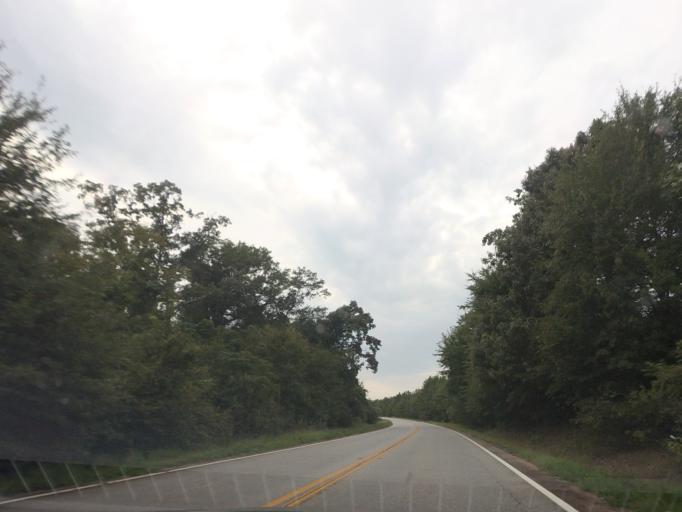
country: US
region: Georgia
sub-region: Twiggs County
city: Jeffersonville
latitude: 32.7470
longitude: -83.4298
